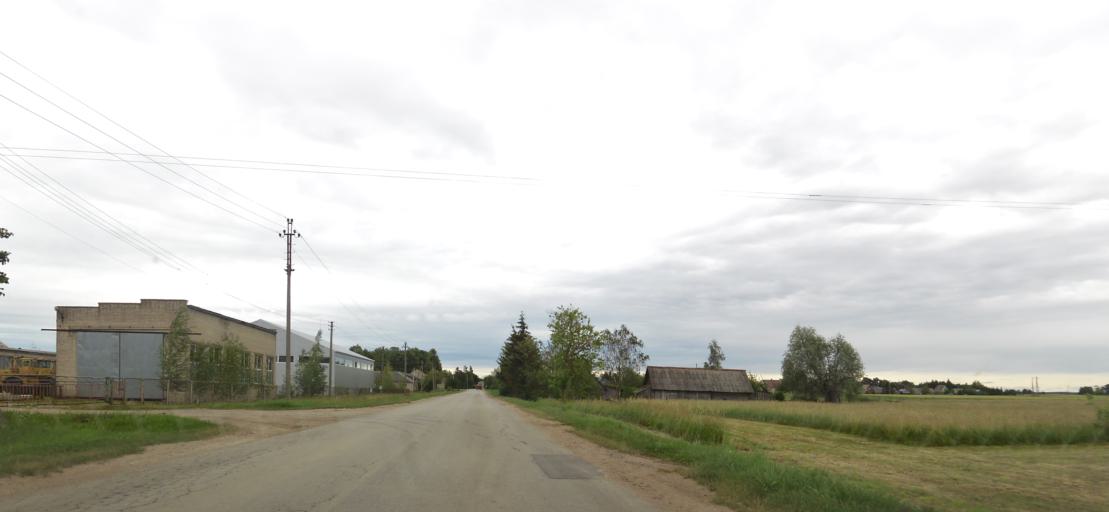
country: LT
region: Panevezys
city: Pasvalys
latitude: 56.0856
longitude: 24.5134
